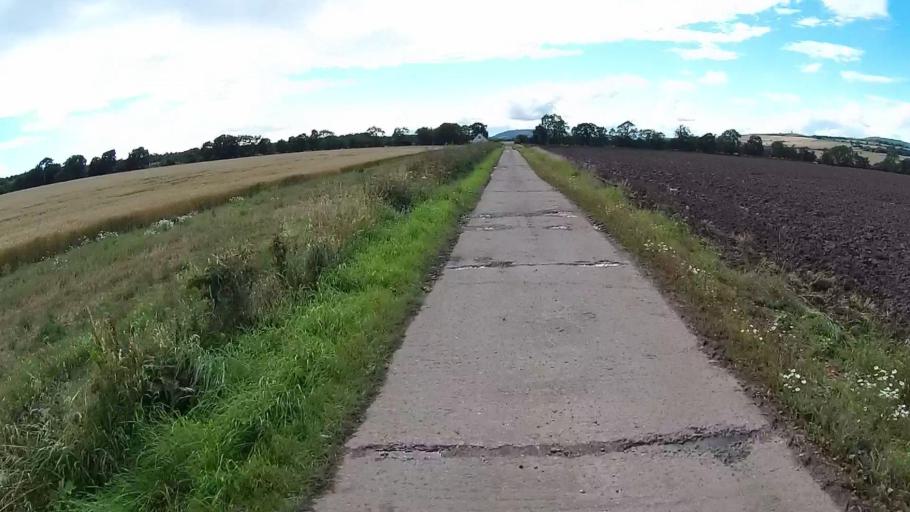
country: GB
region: Scotland
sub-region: Fife
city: Leslie
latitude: 56.1694
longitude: -3.2003
